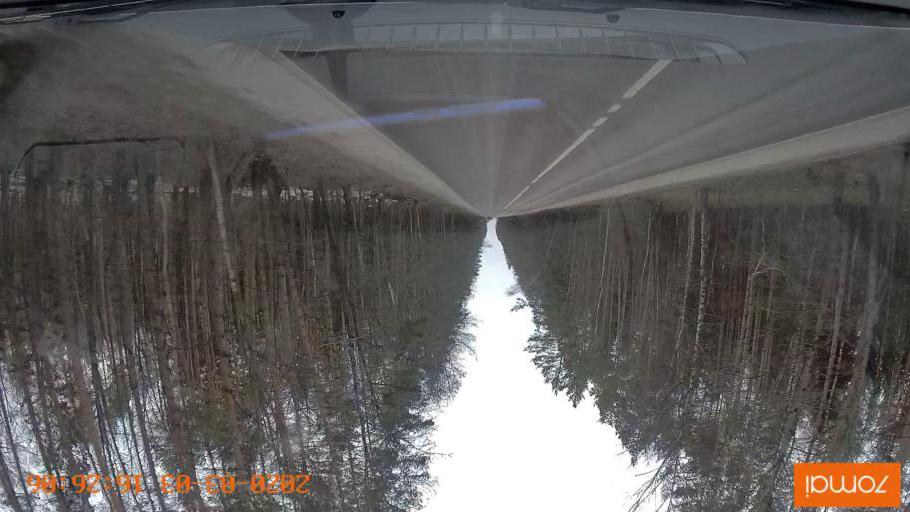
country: RU
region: Moskovskaya
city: Konobeyevo
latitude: 55.4432
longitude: 38.6600
